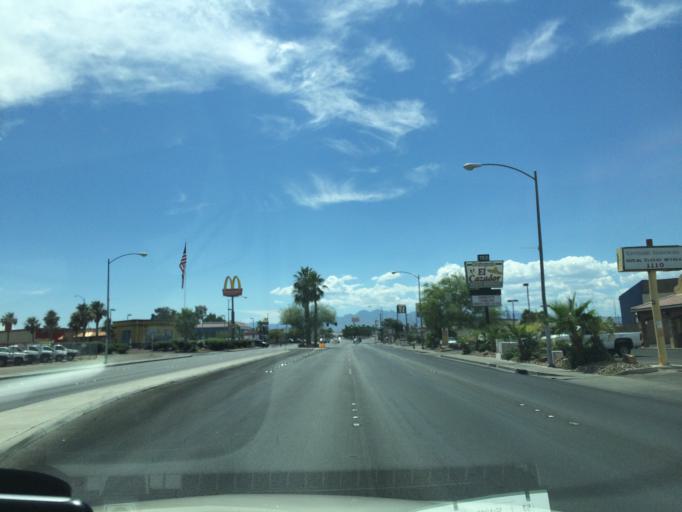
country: US
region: Nevada
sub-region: Clark County
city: North Las Vegas
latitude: 36.1959
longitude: -115.1264
